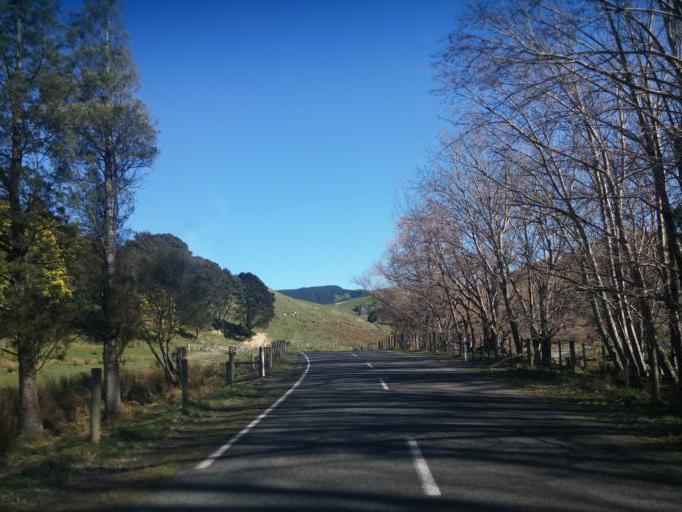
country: NZ
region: Wellington
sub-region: South Wairarapa District
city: Waipawa
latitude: -41.3927
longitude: 175.5103
